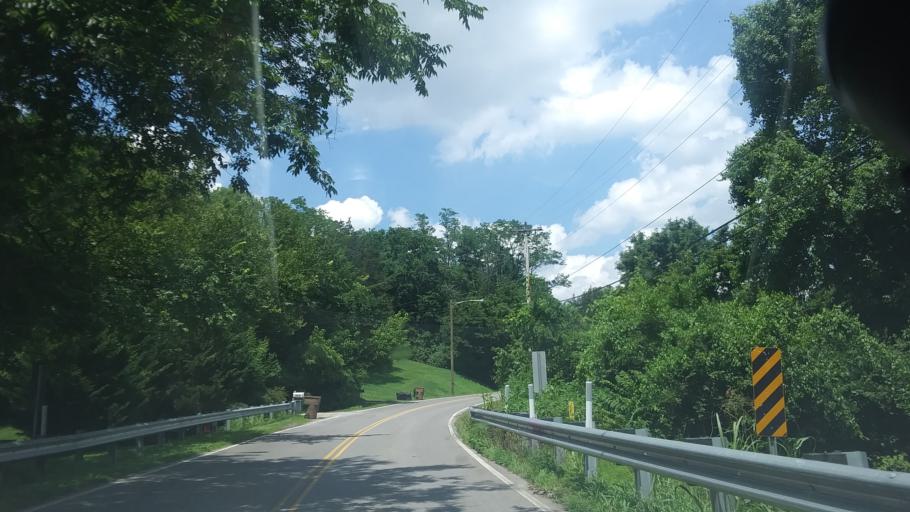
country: US
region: Tennessee
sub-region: Davidson County
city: Oak Hill
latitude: 36.0720
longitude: -86.6989
